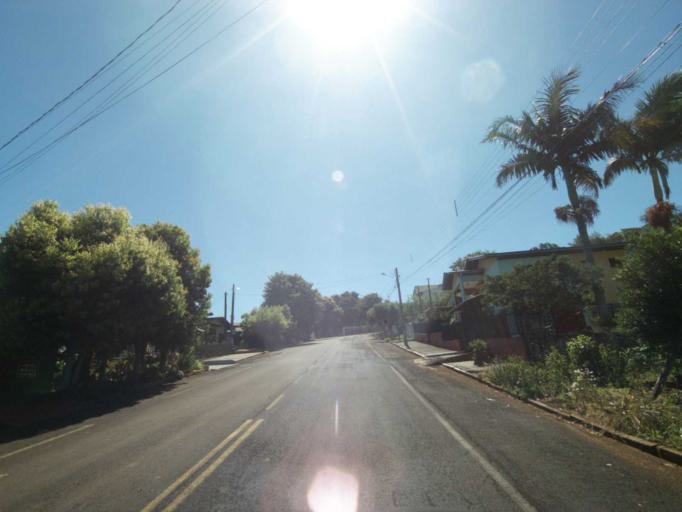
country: BR
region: Parana
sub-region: Coronel Vivida
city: Coronel Vivida
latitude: -25.9609
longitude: -52.8179
